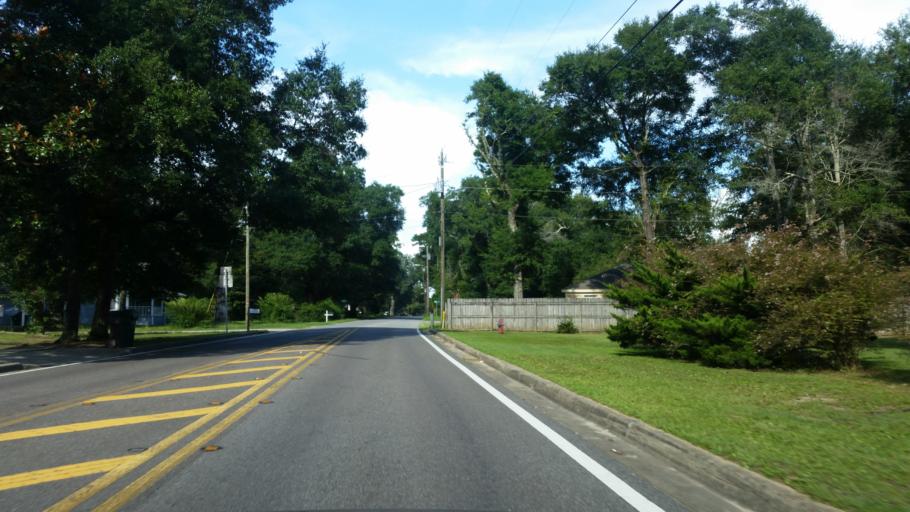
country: US
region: Florida
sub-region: Santa Rosa County
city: Milton
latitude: 30.6235
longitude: -87.0552
